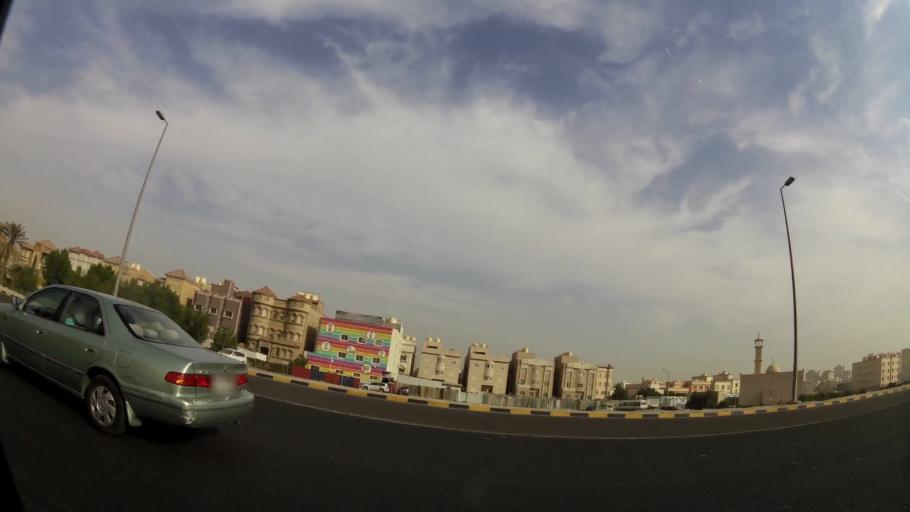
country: KW
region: Al Farwaniyah
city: Al Farwaniyah
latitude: 29.2668
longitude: 47.9447
